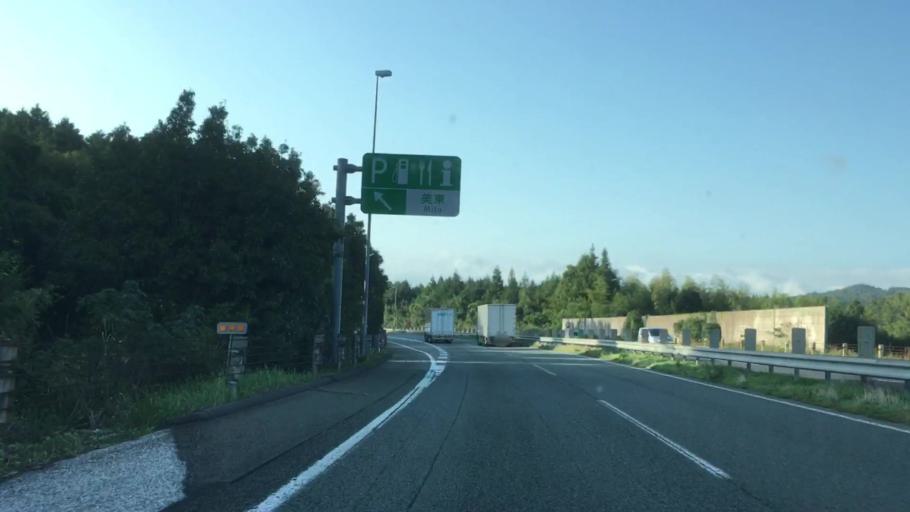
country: JP
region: Yamaguchi
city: Ogori-shimogo
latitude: 34.1506
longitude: 131.3419
